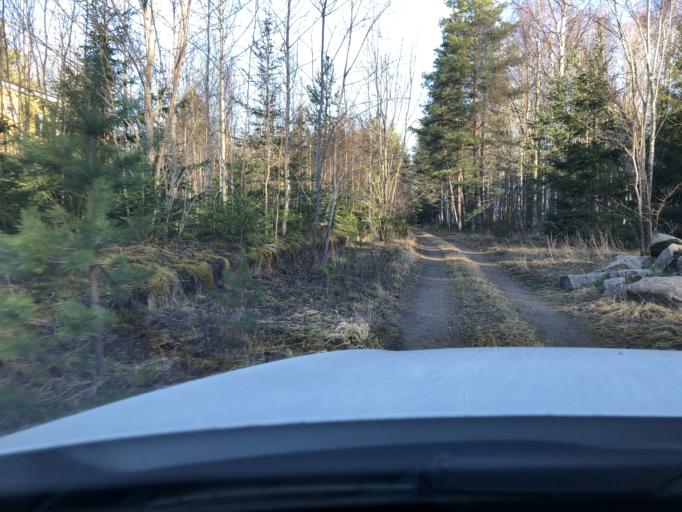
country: SE
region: Gaevleborg
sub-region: Gavle Kommun
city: Hedesunda
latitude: 60.2940
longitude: 16.8954
